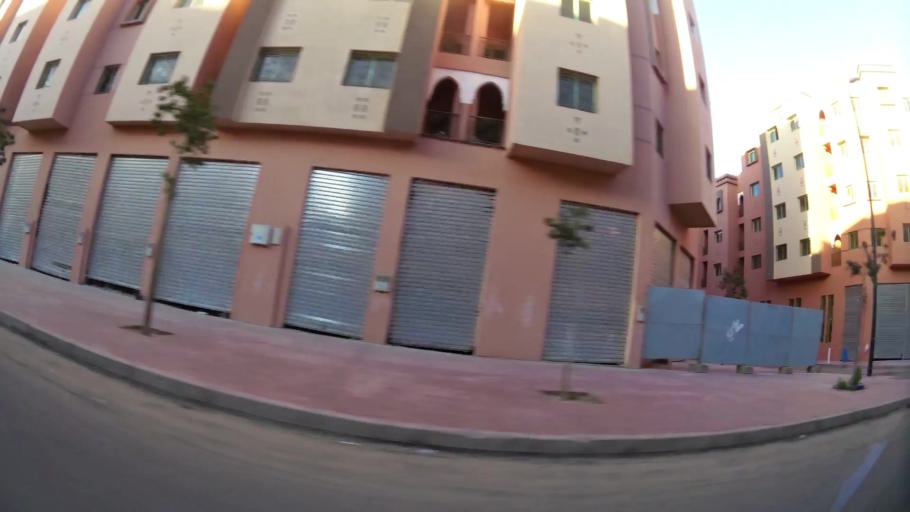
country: MA
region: Marrakech-Tensift-Al Haouz
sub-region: Marrakech
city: Marrakesh
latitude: 31.6490
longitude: -8.0376
